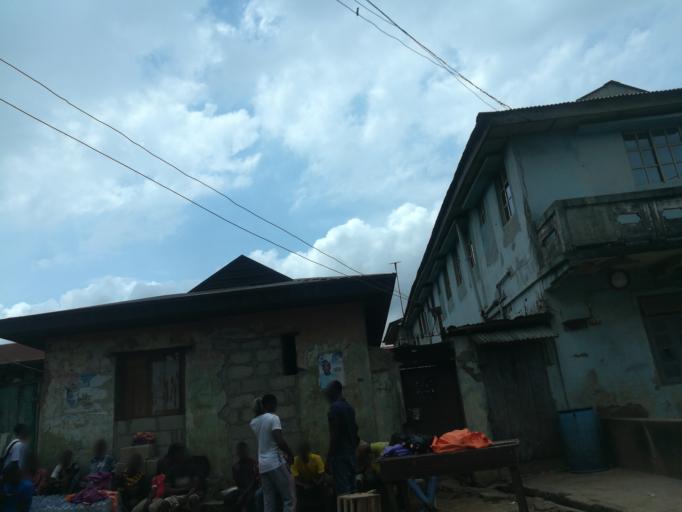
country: NG
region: Lagos
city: Mushin
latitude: 6.5241
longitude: 3.3666
